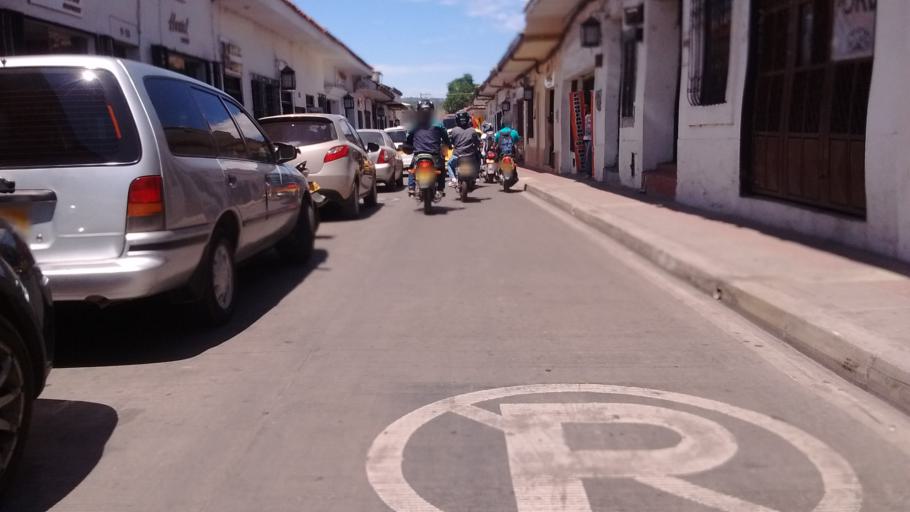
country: CO
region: Cauca
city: Popayan
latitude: 2.4412
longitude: -76.6090
